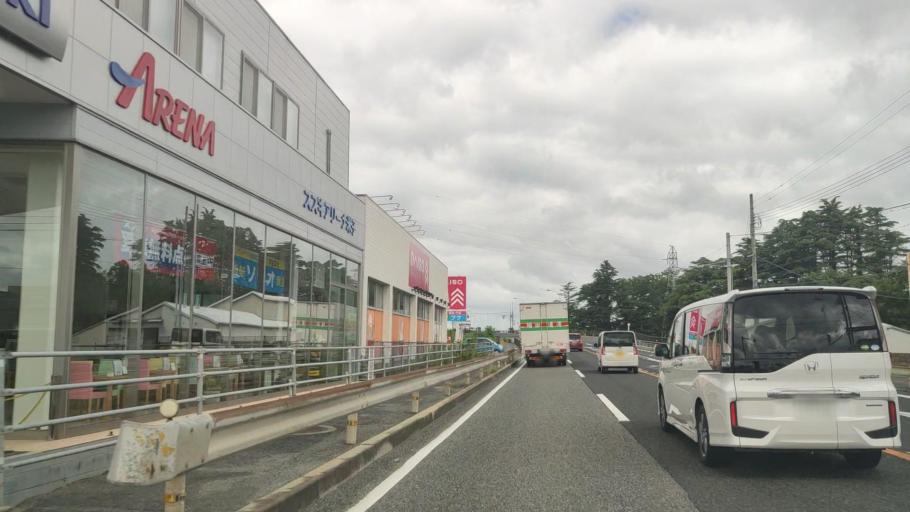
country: JP
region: Tottori
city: Yonago
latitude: 35.4302
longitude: 133.3713
